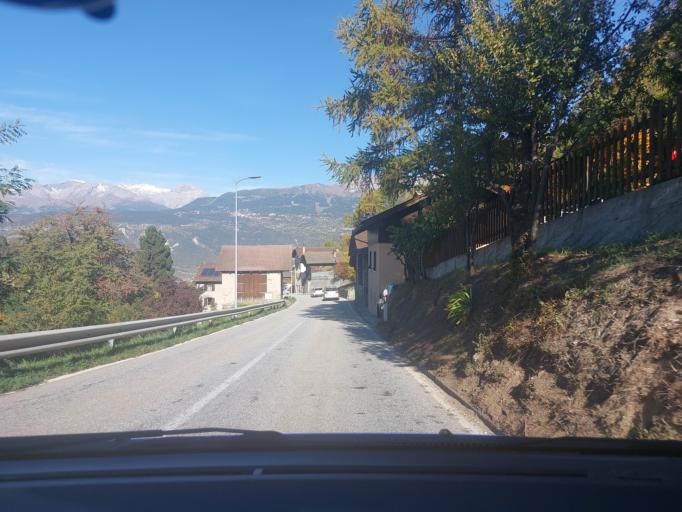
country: CH
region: Valais
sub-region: Sierre District
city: Chippis
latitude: 46.2694
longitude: 7.5536
